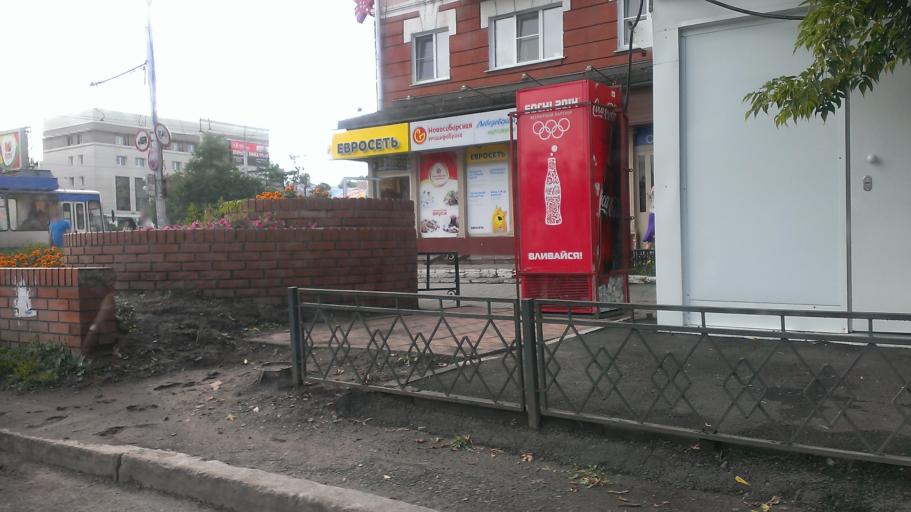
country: RU
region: Altai Krai
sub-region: Gorod Barnaulskiy
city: Barnaul
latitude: 53.3459
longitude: 83.7800
